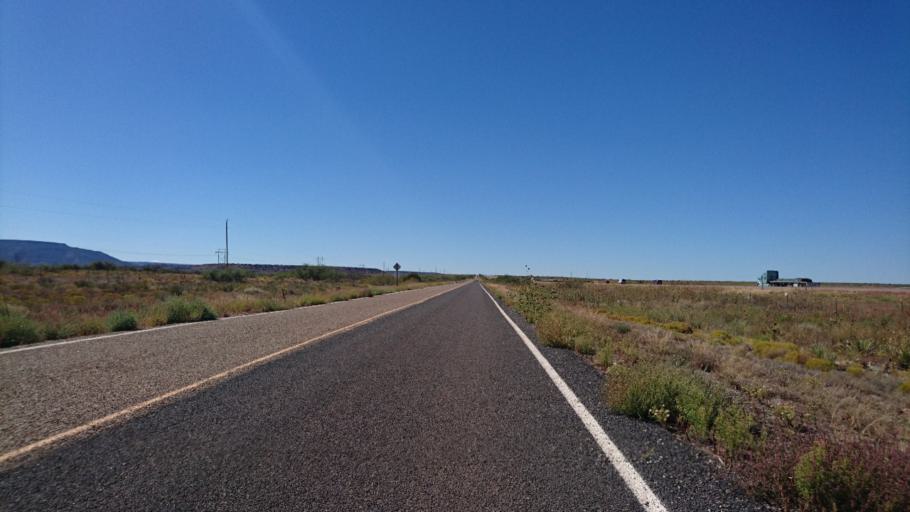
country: US
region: New Mexico
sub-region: Quay County
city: Tucumcari
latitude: 35.0856
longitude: -104.1004
